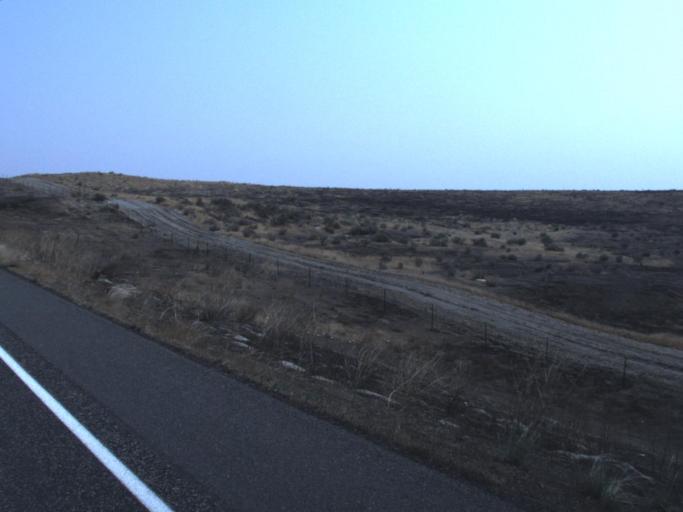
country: US
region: Washington
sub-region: Grant County
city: Desert Aire
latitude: 46.5764
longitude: -119.7365
